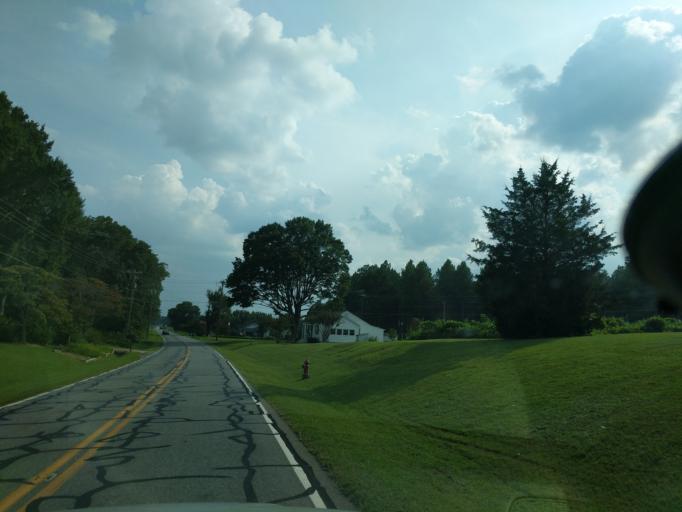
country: US
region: North Carolina
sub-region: Rutherford County
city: Spindale
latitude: 35.2955
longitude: -81.9428
